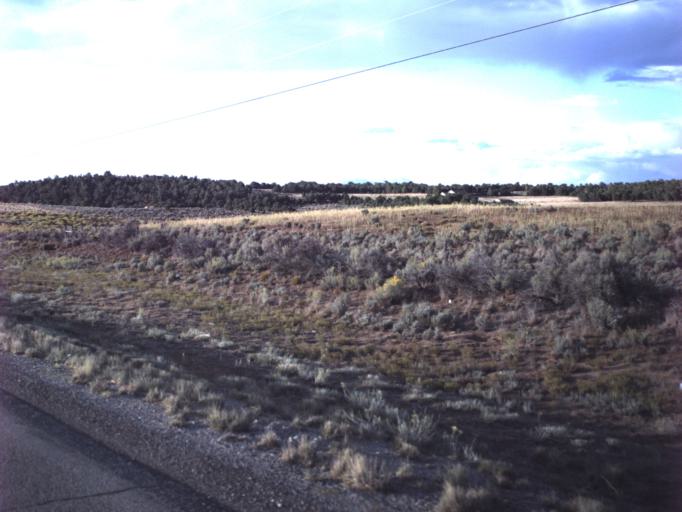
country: US
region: Utah
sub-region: San Juan County
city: Monticello
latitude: 37.9601
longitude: -109.3531
